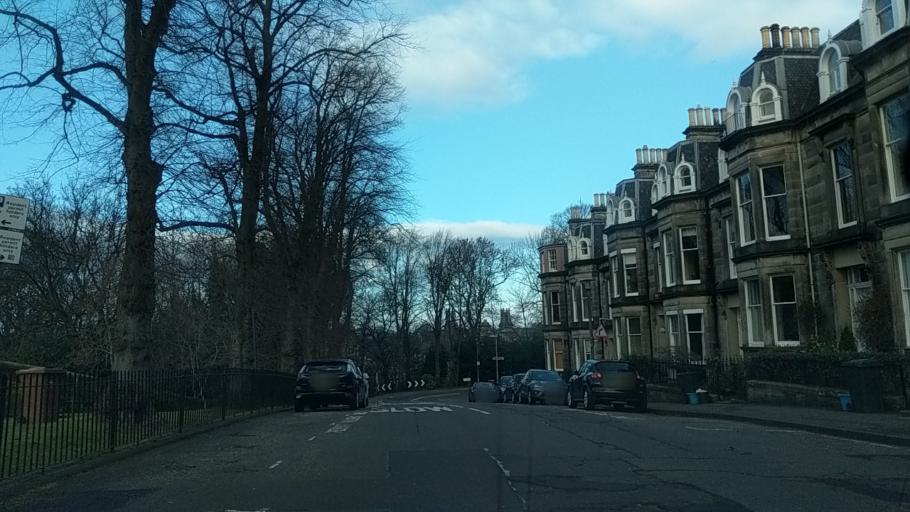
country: GB
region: Scotland
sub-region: Edinburgh
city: Edinburgh
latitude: 55.9481
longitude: -3.2233
